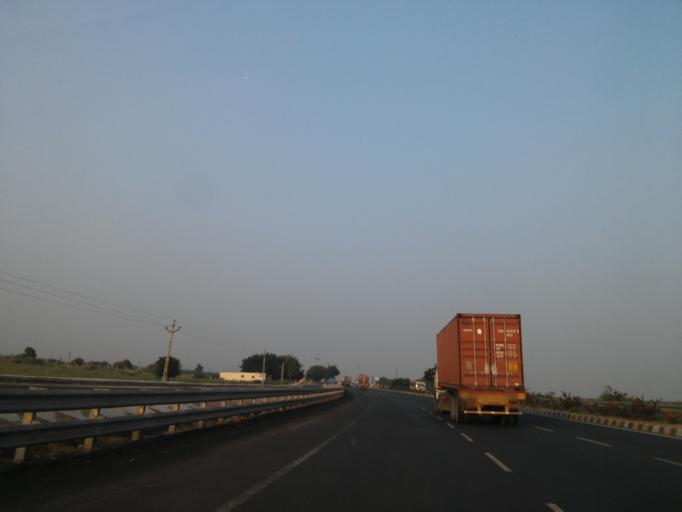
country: IN
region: Gujarat
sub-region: Kachchh
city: Bhachau
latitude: 23.3115
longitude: 70.4746
